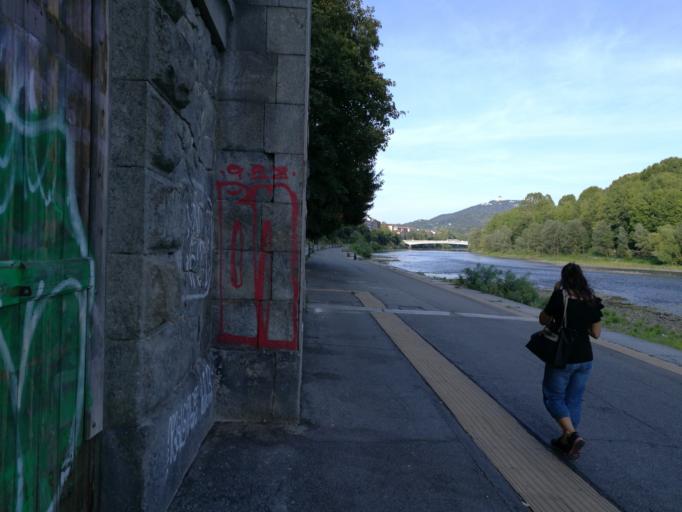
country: IT
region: Piedmont
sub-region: Provincia di Torino
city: Turin
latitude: 45.0655
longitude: 7.6988
